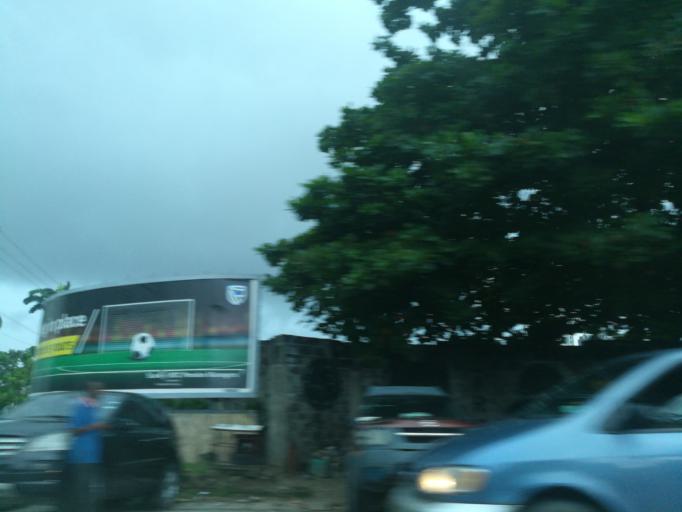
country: NG
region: Lagos
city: Ikoyi
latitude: 6.4246
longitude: 3.4241
